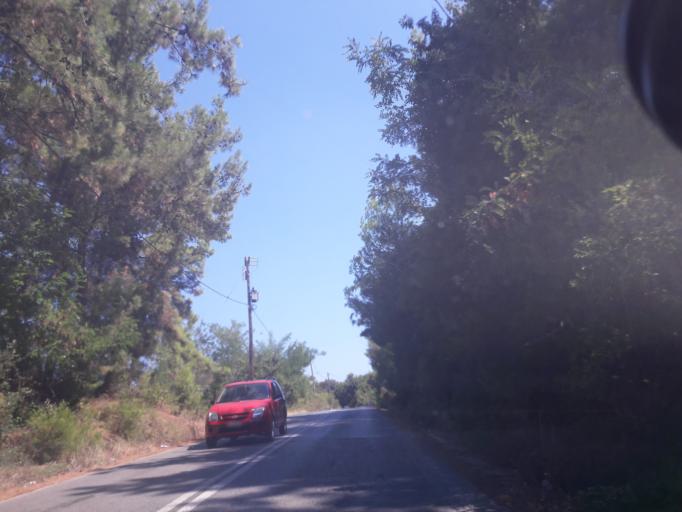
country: GR
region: Central Macedonia
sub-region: Nomos Chalkidikis
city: Nea Roda
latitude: 40.3848
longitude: 23.8983
